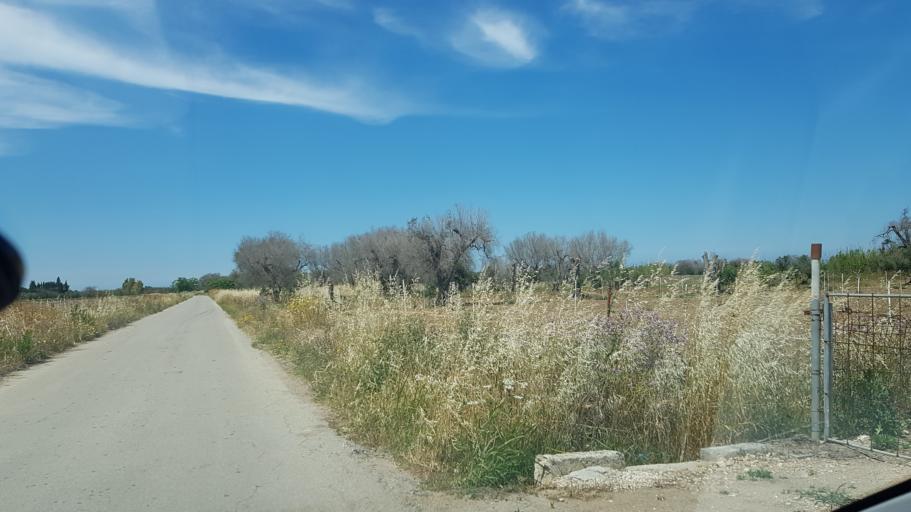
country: IT
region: Apulia
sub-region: Provincia di Brindisi
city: San Pietro Vernotico
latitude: 40.5194
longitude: 18.0123
